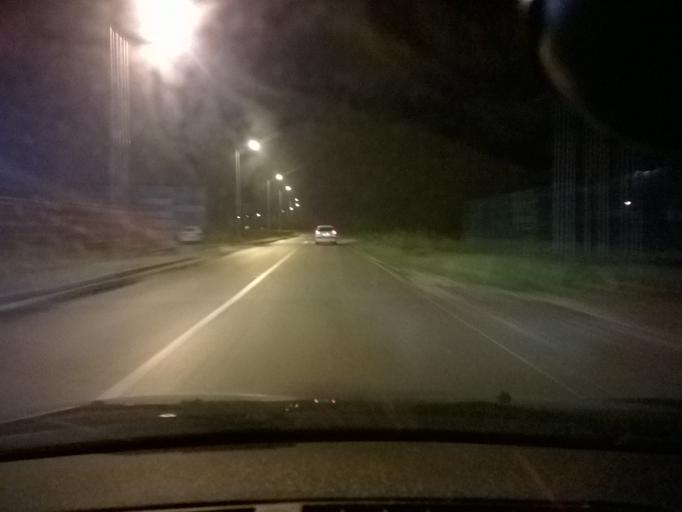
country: HR
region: Krapinsko-Zagorska
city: Zabok
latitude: 46.0722
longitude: 15.9071
